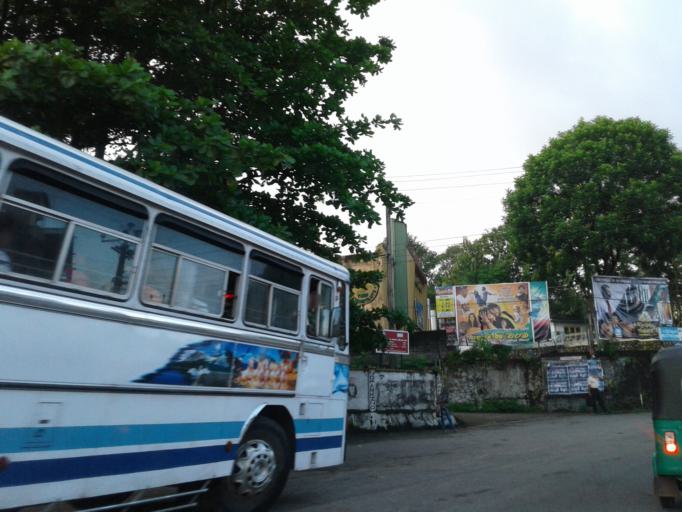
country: LK
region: Western
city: Mulleriyawa
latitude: 6.9346
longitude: 79.9838
